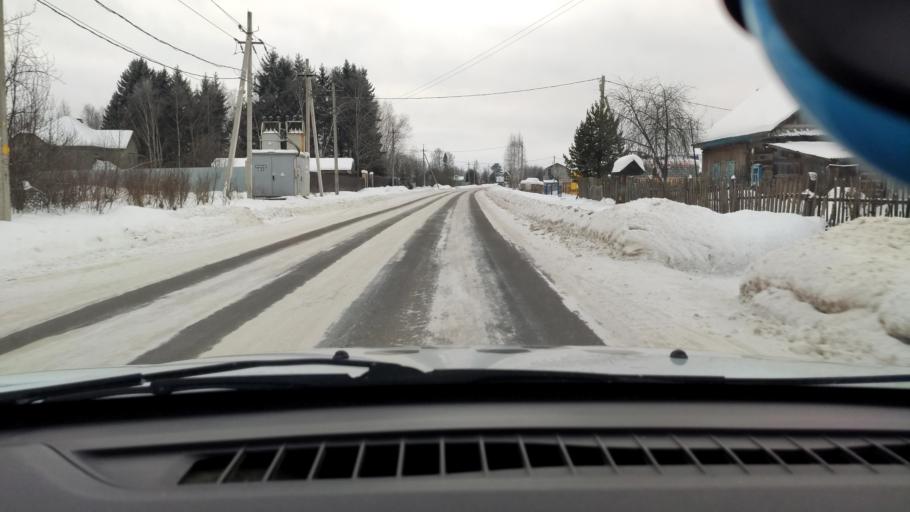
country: RU
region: Perm
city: Overyata
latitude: 58.0744
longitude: 55.9598
